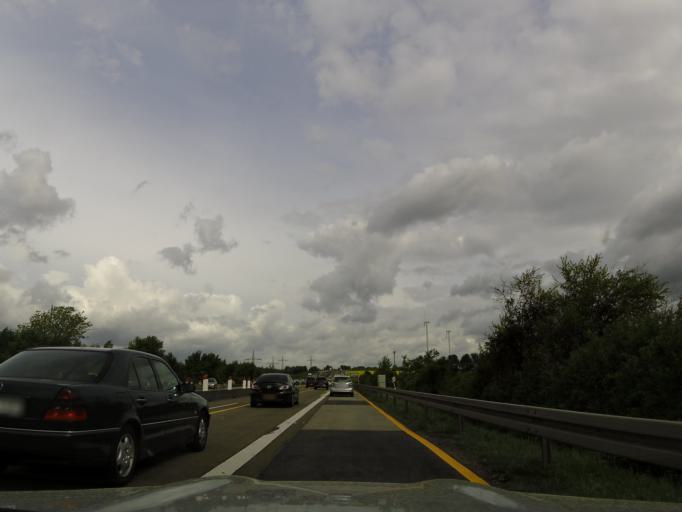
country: DE
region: Hesse
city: Bad Camberg
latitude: 50.2722
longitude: 8.2467
